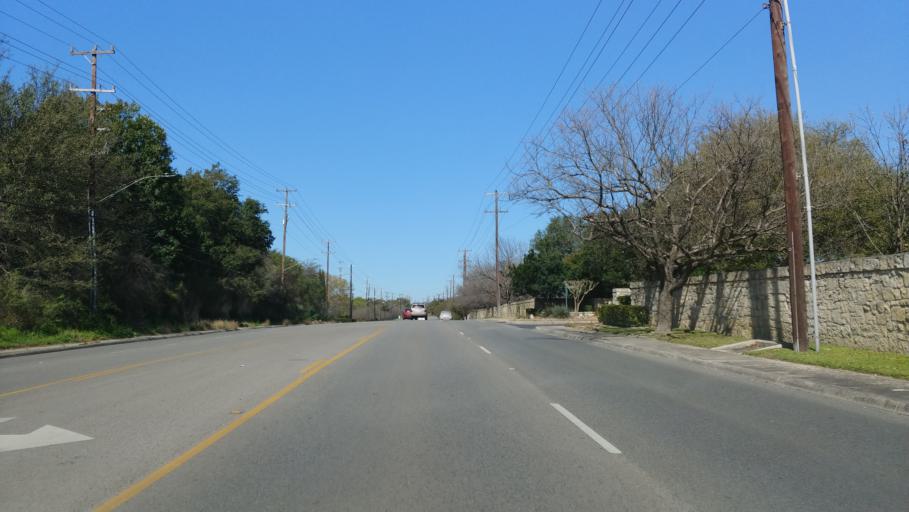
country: US
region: Texas
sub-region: Bexar County
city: Shavano Park
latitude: 29.5663
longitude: -98.5600
